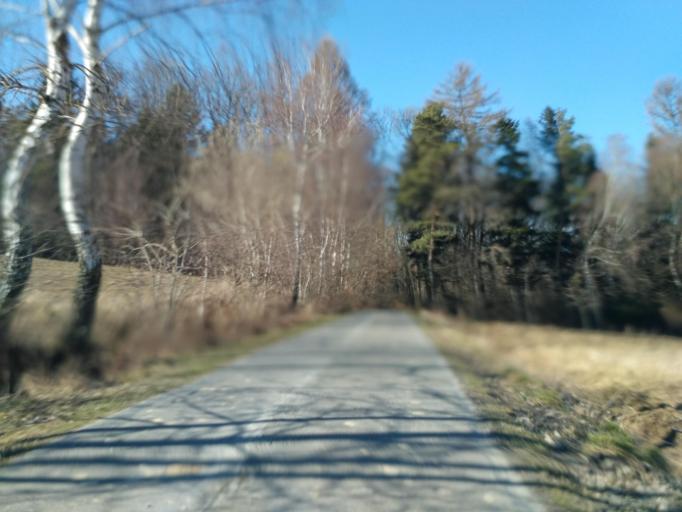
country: PL
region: Subcarpathian Voivodeship
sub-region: Powiat ropczycko-sedziszowski
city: Wielopole Skrzynskie
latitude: 49.9524
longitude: 21.5840
